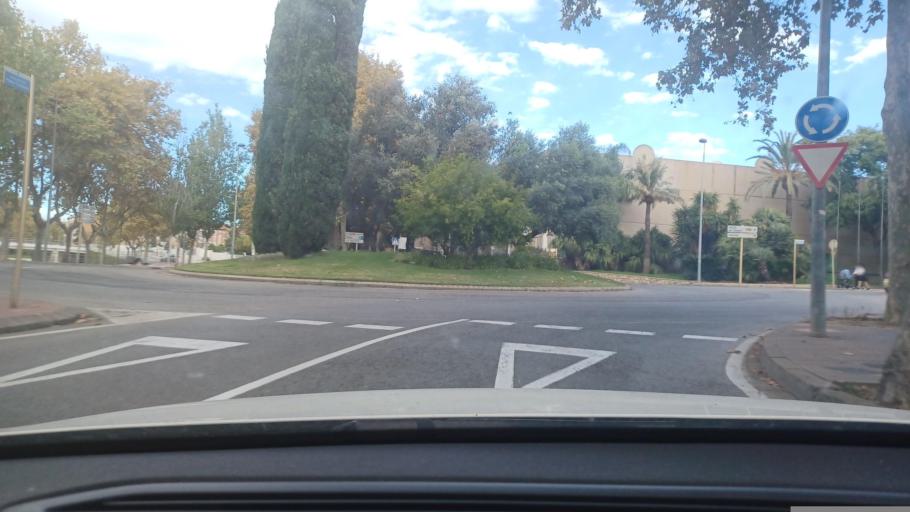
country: ES
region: Catalonia
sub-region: Provincia de Tarragona
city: Cambrils
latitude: 41.0710
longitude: 1.0563
